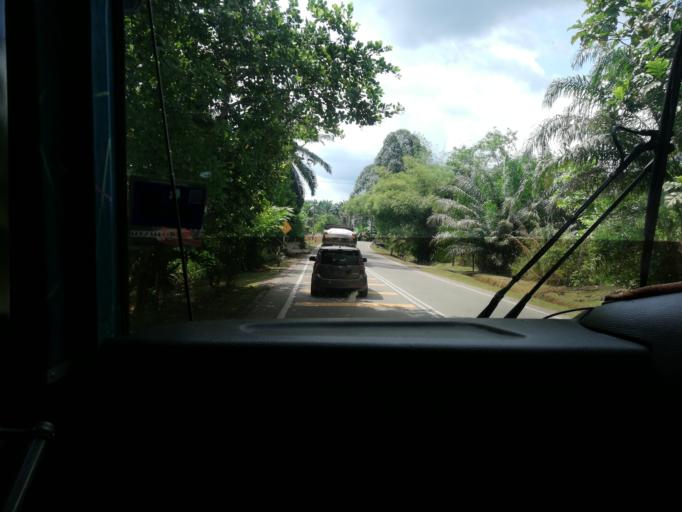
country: MY
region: Penang
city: Nibong Tebal
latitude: 5.2193
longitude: 100.6091
